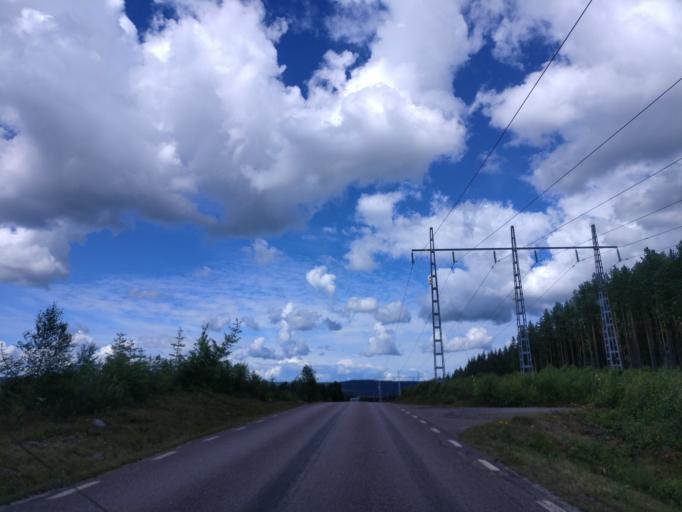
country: SE
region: Vaermland
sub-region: Hagfors Kommun
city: Hagfors
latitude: 60.0407
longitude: 13.5365
